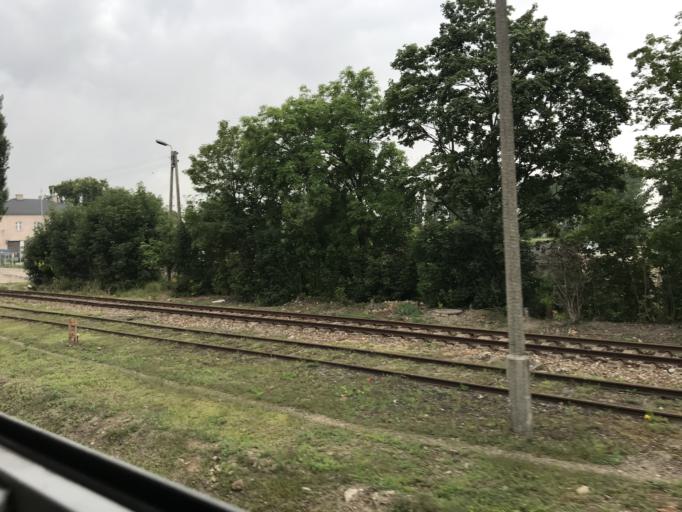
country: PL
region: Pomeranian Voivodeship
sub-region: Powiat tczewski
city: Tczew
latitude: 54.0931
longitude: 18.8016
